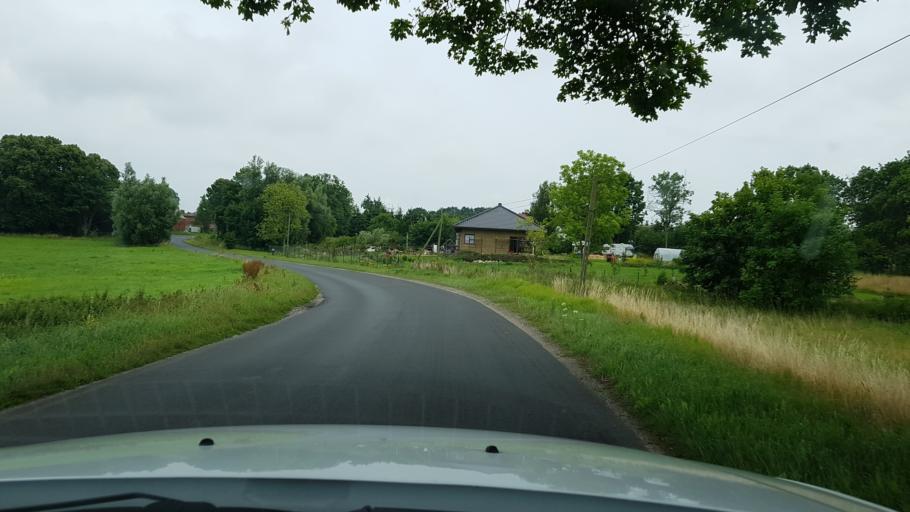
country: PL
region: West Pomeranian Voivodeship
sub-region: Powiat slawienski
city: Slawno
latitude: 54.4910
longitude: 16.5795
